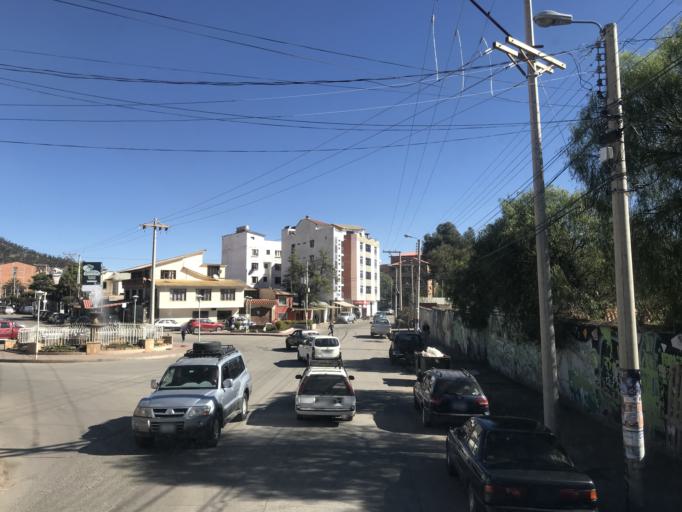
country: BO
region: Chuquisaca
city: Sucre
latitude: -19.0405
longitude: -65.2445
